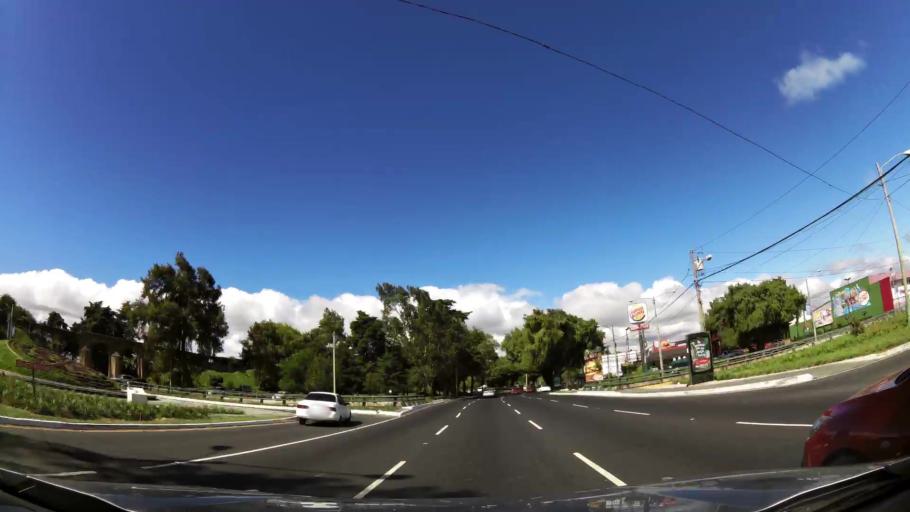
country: GT
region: Guatemala
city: Santa Catarina Pinula
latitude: 14.5962
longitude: -90.5214
